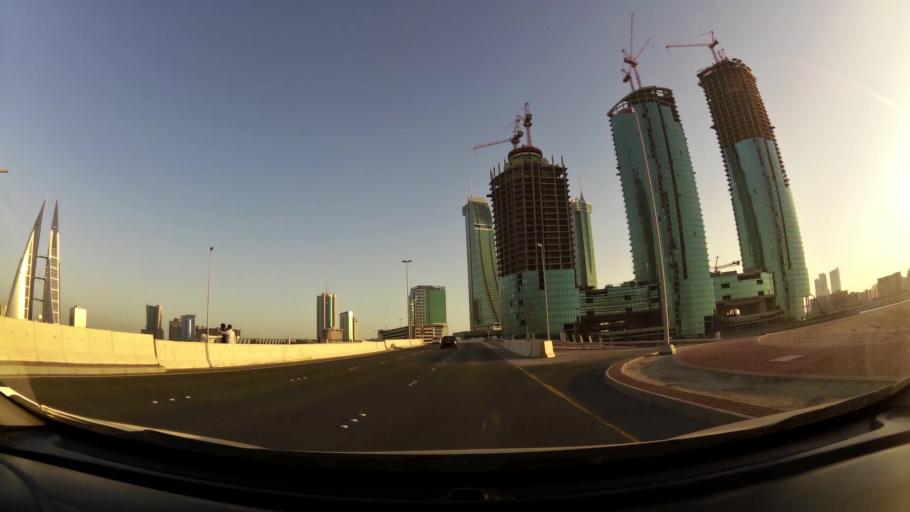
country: BH
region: Manama
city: Manama
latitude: 26.2433
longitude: 50.5744
